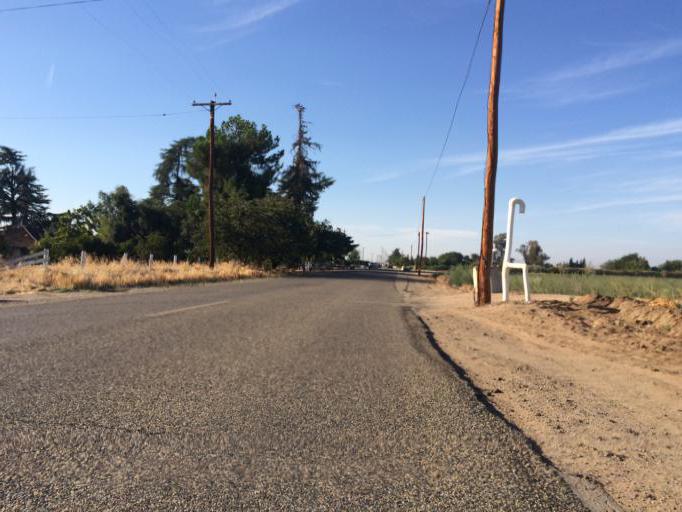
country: US
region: California
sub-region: Fresno County
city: Sunnyside
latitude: 36.7636
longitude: -119.6731
